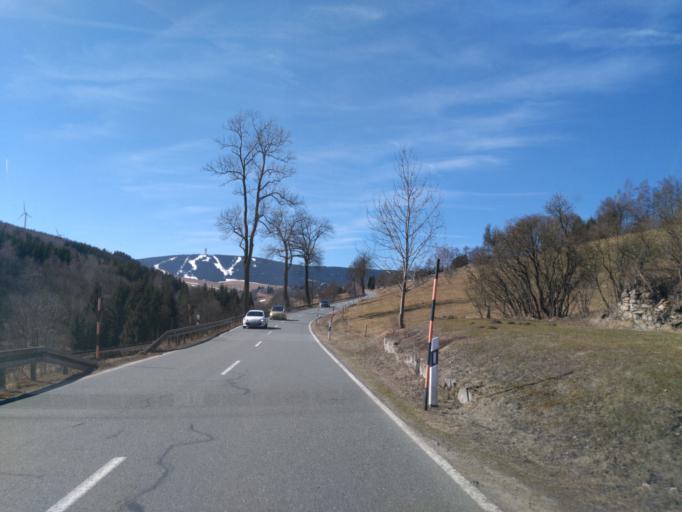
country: DE
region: Saxony
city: Kurort Oberwiesenthal
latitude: 50.4357
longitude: 12.9976
